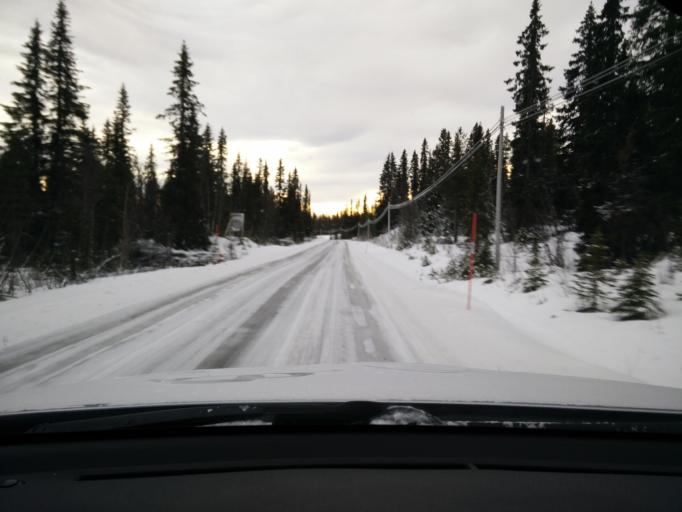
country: SE
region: Jaemtland
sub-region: Bergs Kommun
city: Hoverberg
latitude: 62.4839
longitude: 14.1211
